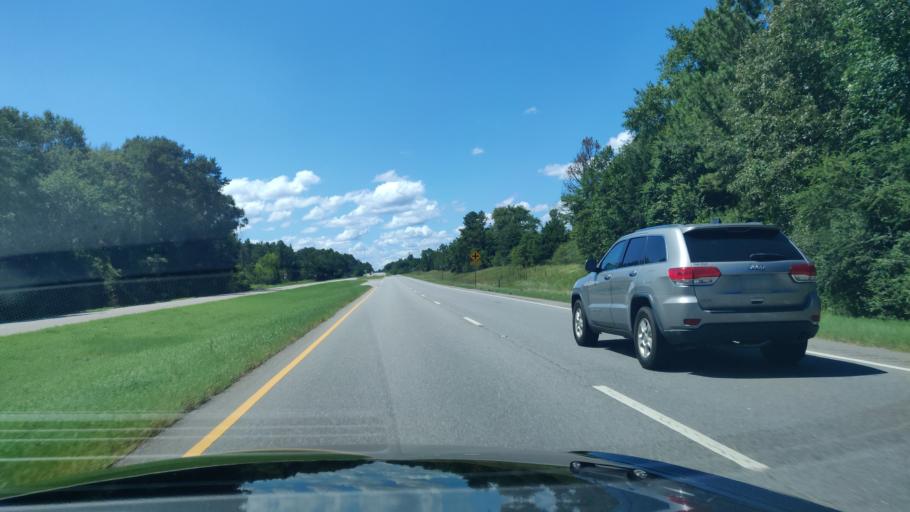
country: US
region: Georgia
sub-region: Terrell County
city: Dawson
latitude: 31.8827
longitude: -84.5030
